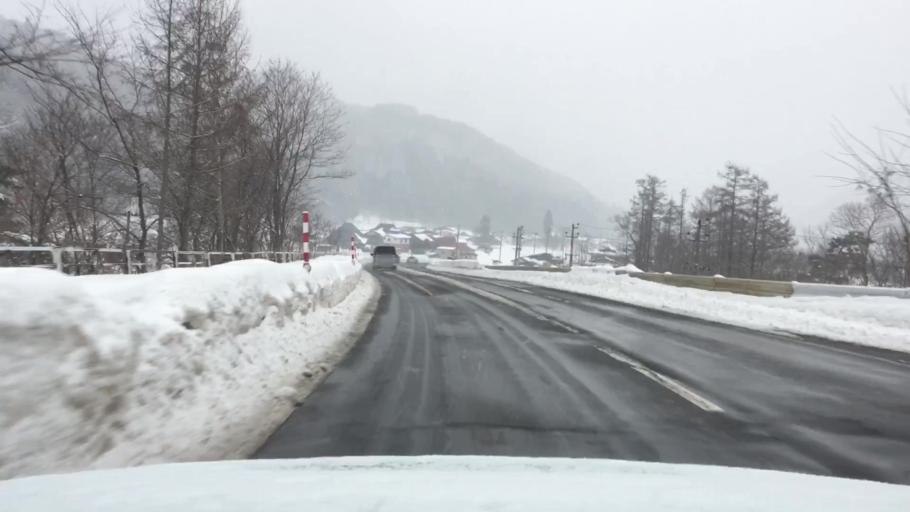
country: JP
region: Akita
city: Hanawa
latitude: 40.0638
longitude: 141.0154
